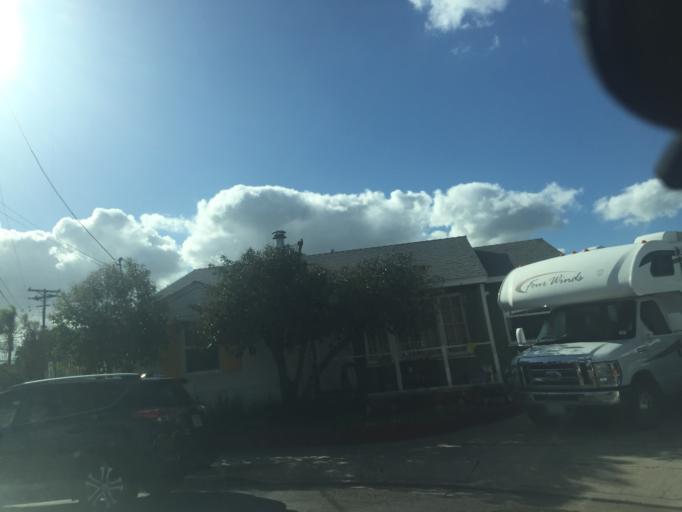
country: US
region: California
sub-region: San Diego County
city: La Mesa
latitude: 32.7901
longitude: -117.0846
